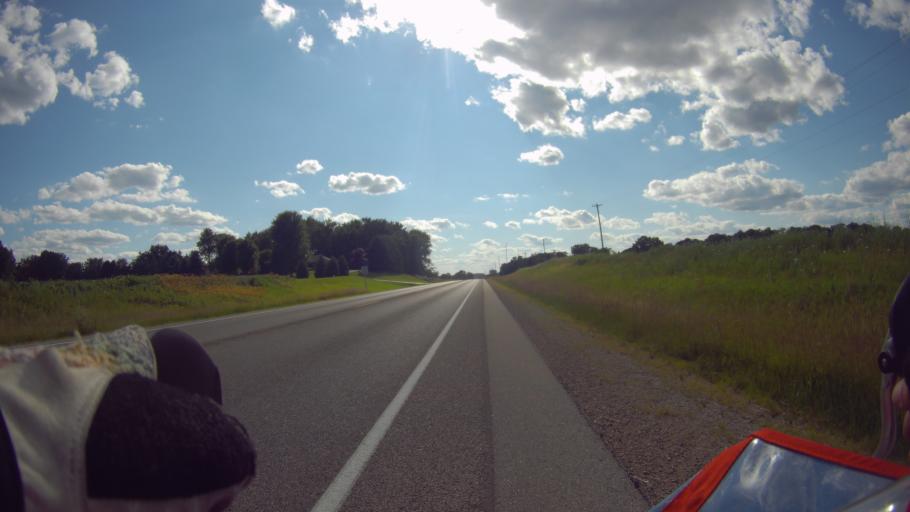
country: US
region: Wisconsin
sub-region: Dane County
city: Stoughton
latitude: 42.9189
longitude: -89.2826
